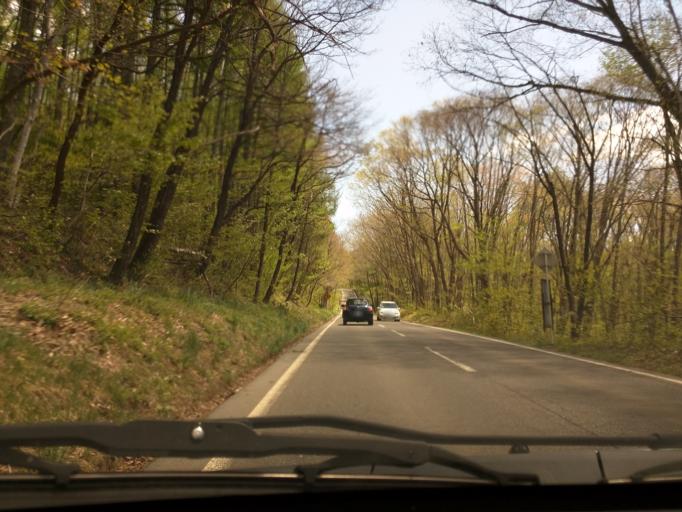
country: JP
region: Nagano
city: Nagano-shi
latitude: 36.7160
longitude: 138.1092
